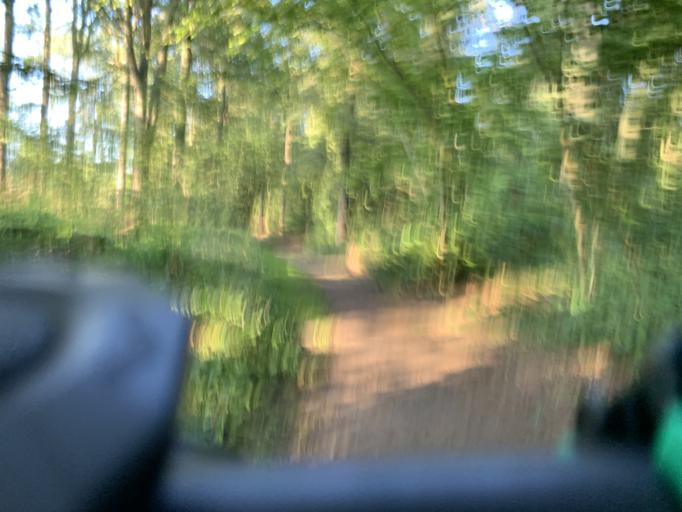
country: DE
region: Lower Saxony
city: Westerstede
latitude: 53.2550
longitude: 7.9107
